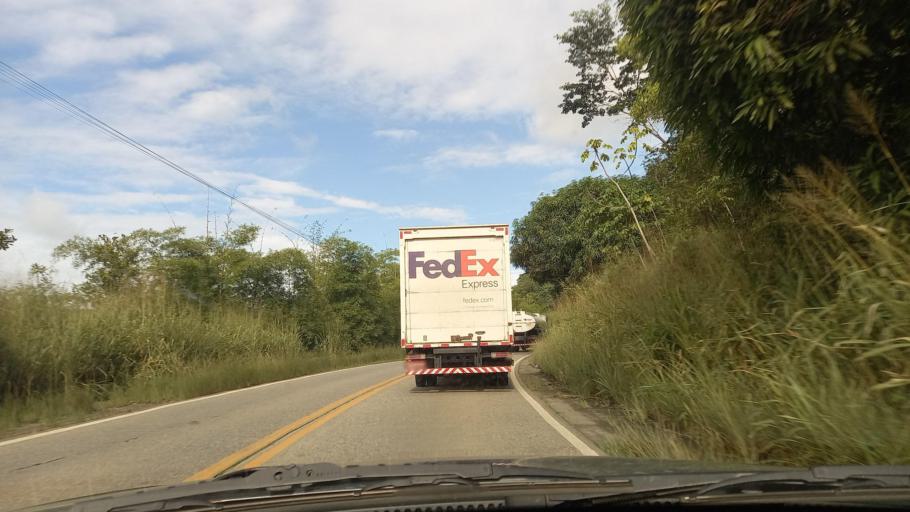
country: BR
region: Pernambuco
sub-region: Catende
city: Catende
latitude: -8.6899
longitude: -35.6713
